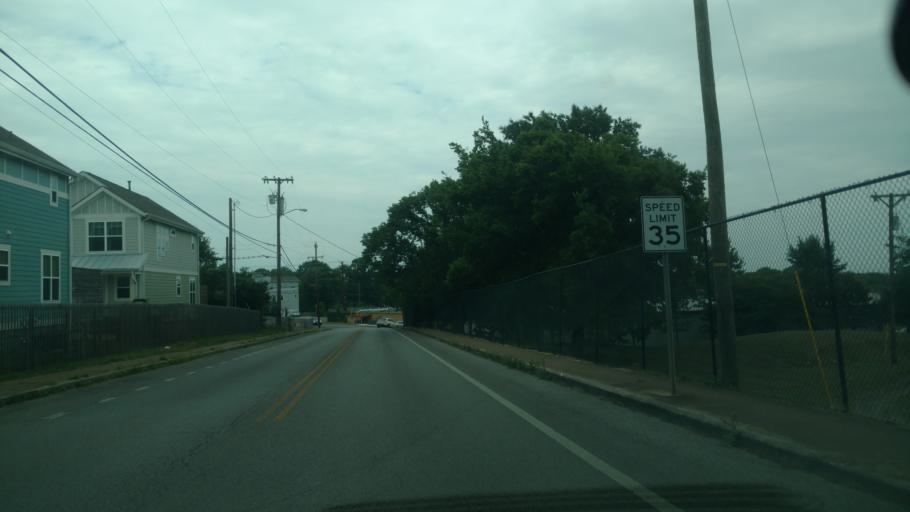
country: US
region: Tennessee
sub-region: Davidson County
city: Nashville
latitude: 36.1950
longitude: -86.7273
